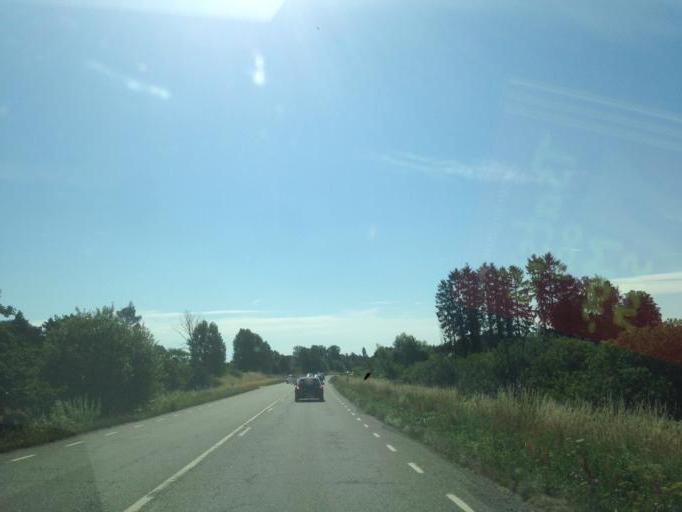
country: SE
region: Skane
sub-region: Simrishamns Kommun
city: Kivik
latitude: 55.6326
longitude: 14.2494
